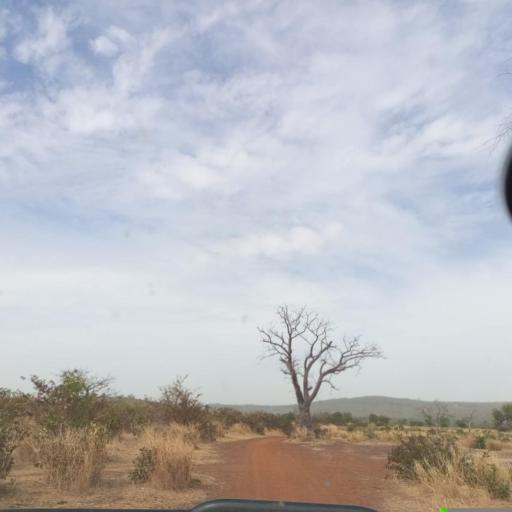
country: ML
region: Koulikoro
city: Koulikoro
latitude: 13.1716
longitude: -7.7337
